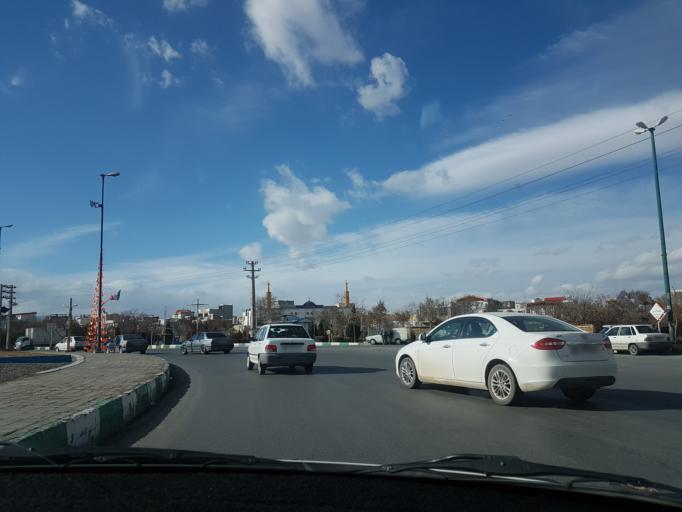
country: IR
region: Markazi
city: Arak
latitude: 34.1197
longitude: 49.7056
